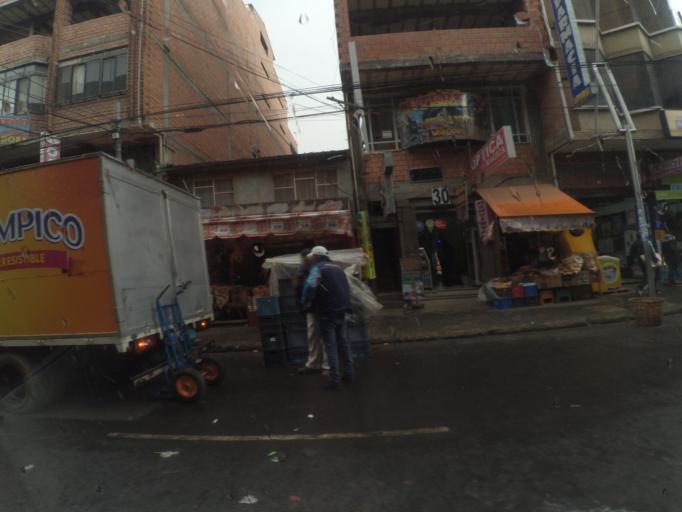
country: BO
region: La Paz
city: La Paz
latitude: -16.5056
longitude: -68.1618
